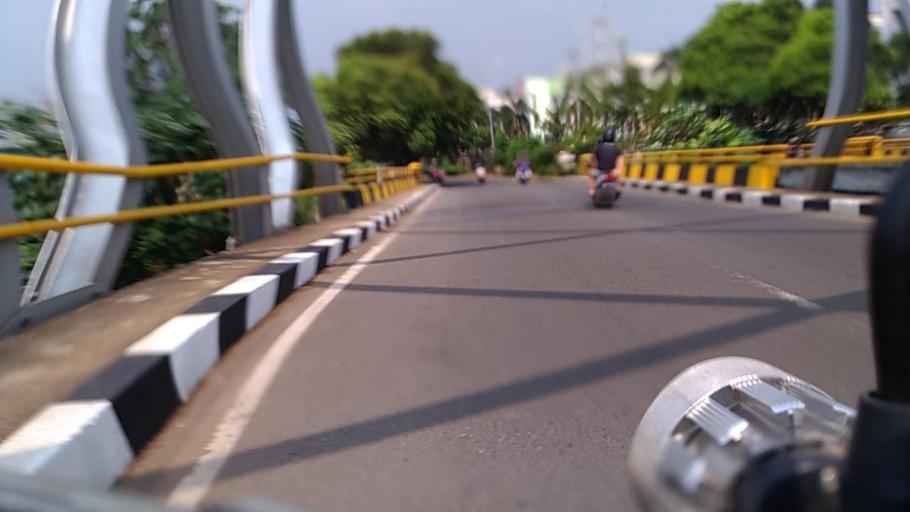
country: ID
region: West Java
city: Depok
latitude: -6.3796
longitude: 106.8391
